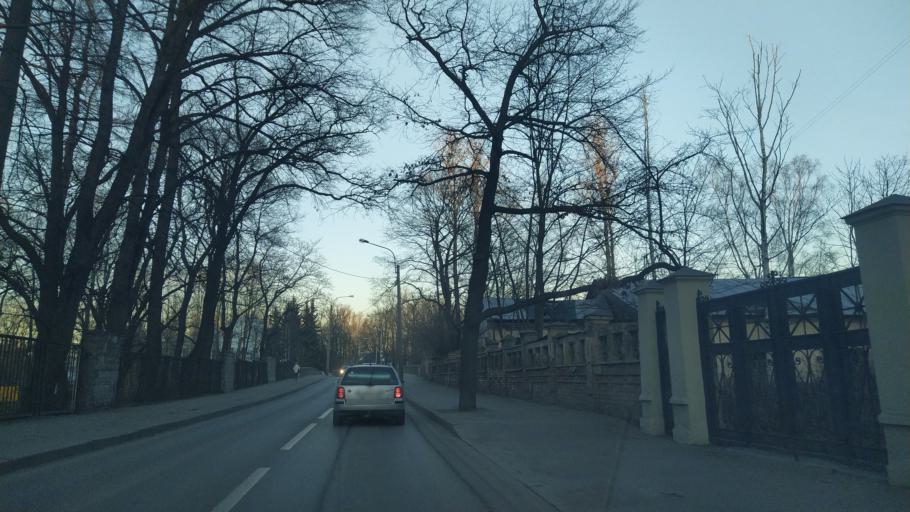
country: RU
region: St.-Petersburg
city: Novaya Derevnya
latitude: 59.9724
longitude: 30.2817
